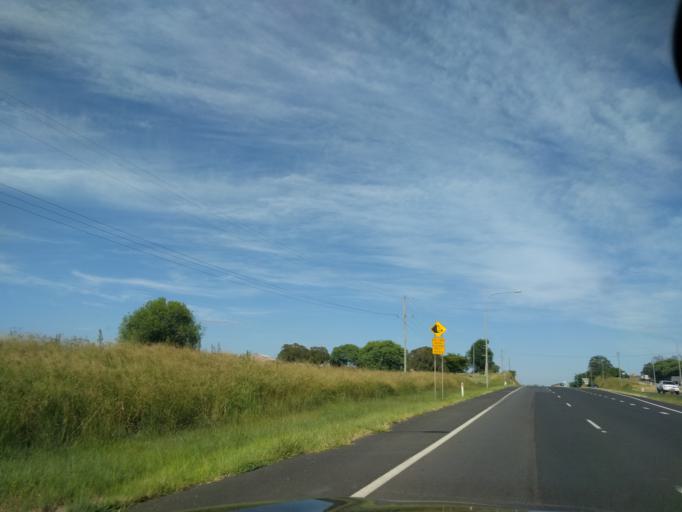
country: AU
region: Queensland
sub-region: Ipswich
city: Thagoona
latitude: -27.5671
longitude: 152.6147
